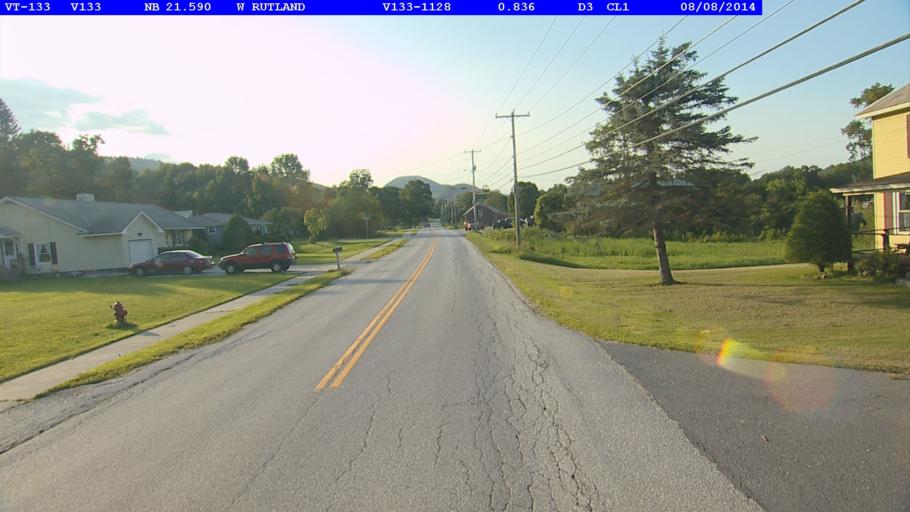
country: US
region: Vermont
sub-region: Rutland County
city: West Rutland
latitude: 43.5812
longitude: -73.0408
